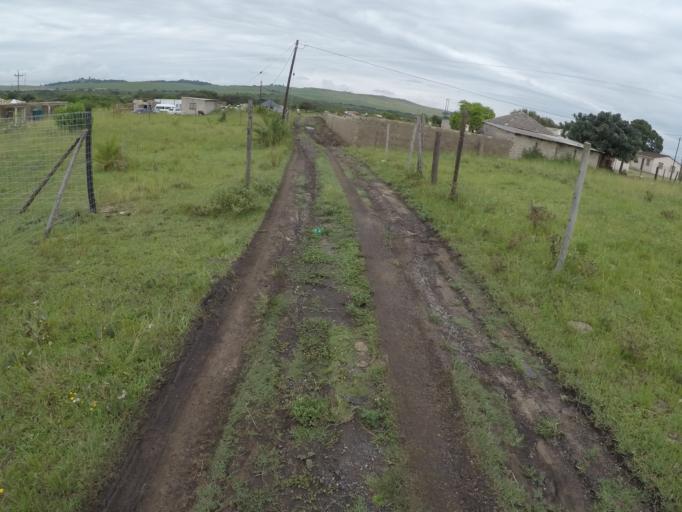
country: ZA
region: KwaZulu-Natal
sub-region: uThungulu District Municipality
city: Empangeni
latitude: -28.7118
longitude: 31.8646
